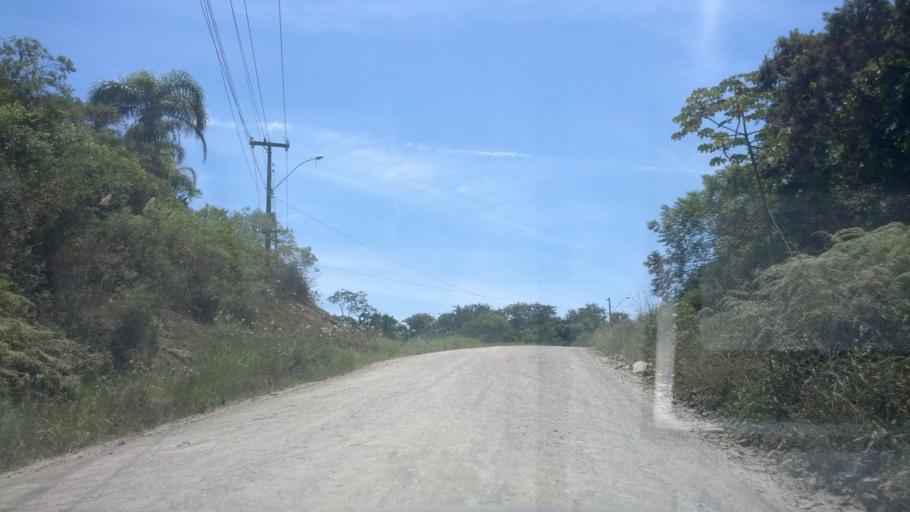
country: BR
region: Santa Catarina
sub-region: Porto Belo
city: Porto Belo
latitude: -27.1638
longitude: -48.5299
